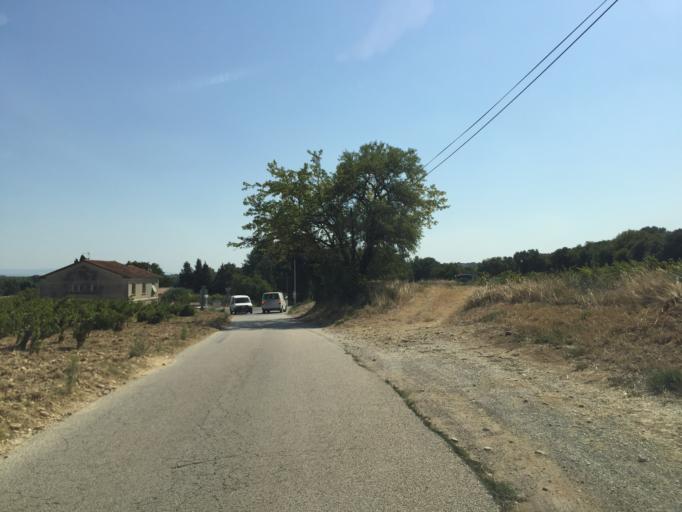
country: FR
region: Provence-Alpes-Cote d'Azur
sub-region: Departement du Vaucluse
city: Courthezon
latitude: 44.0980
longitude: 4.8529
